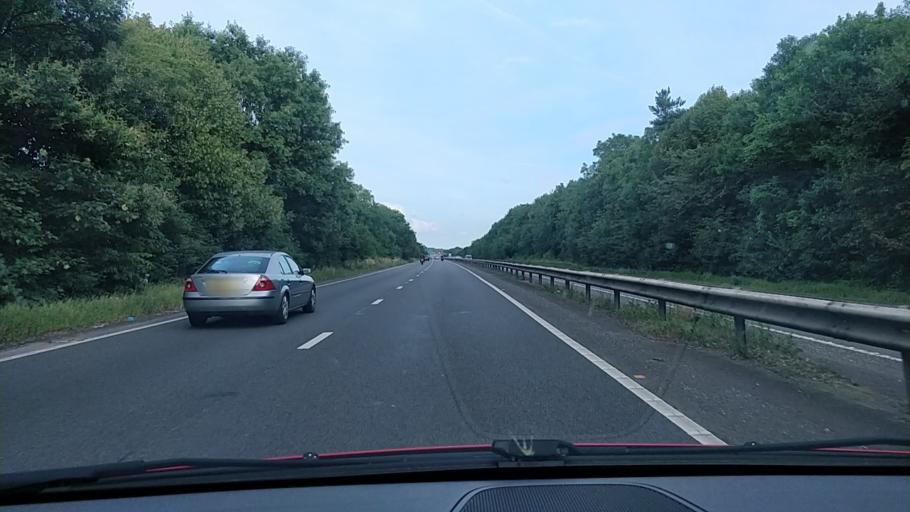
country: GB
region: Wales
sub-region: Wrexham
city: Rossett
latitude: 53.1610
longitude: -2.9572
